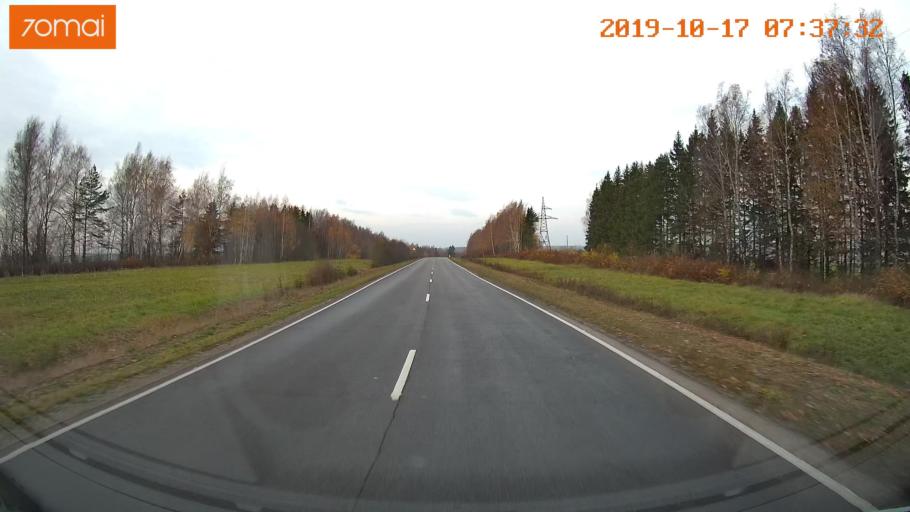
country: RU
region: Vladimir
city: Yur'yev-Pol'skiy
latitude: 56.4499
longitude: 39.8968
